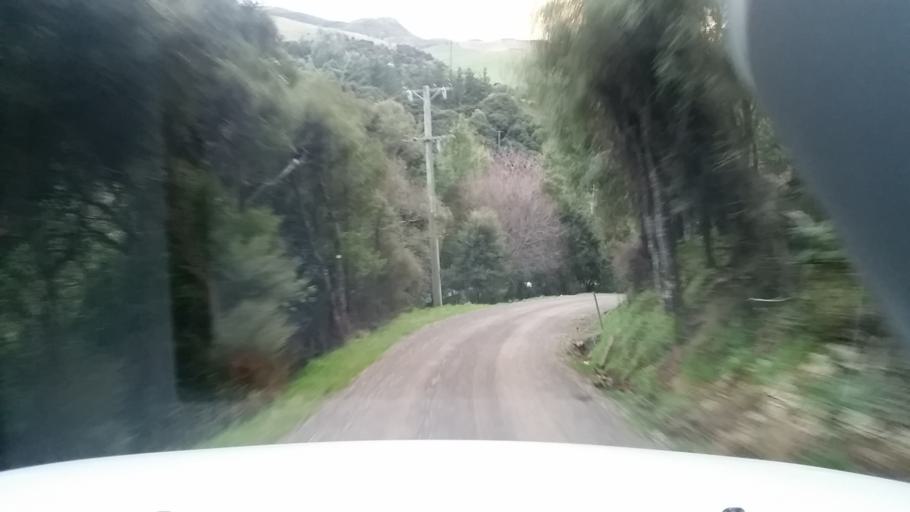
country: NZ
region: Canterbury
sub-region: Christchurch City
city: Christchurch
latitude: -43.7349
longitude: 172.7833
